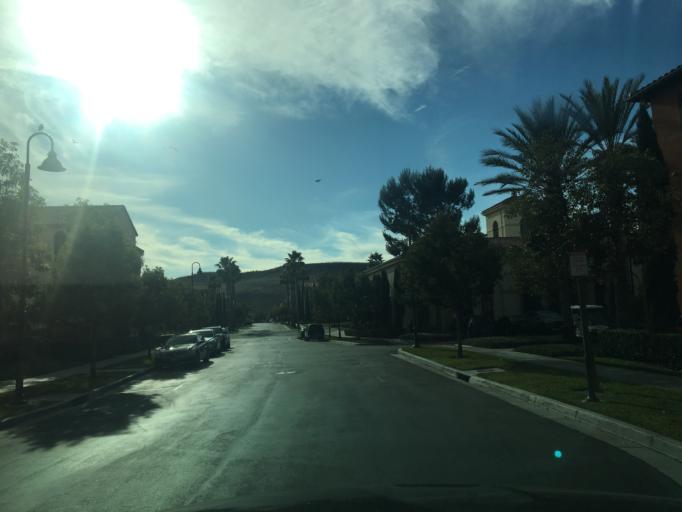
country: US
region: California
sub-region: Orange County
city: Laguna Woods
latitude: 33.6446
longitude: -117.7474
